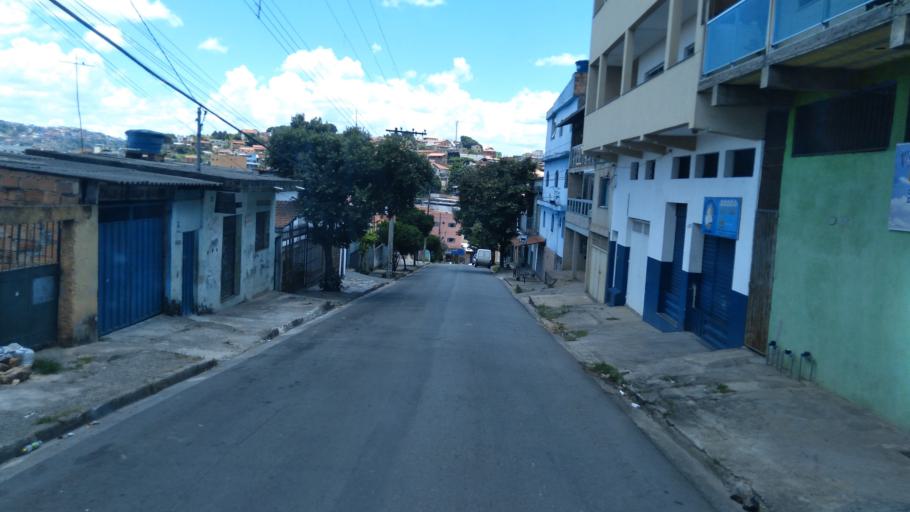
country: BR
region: Minas Gerais
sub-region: Belo Horizonte
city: Belo Horizonte
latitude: -19.8523
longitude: -43.8972
